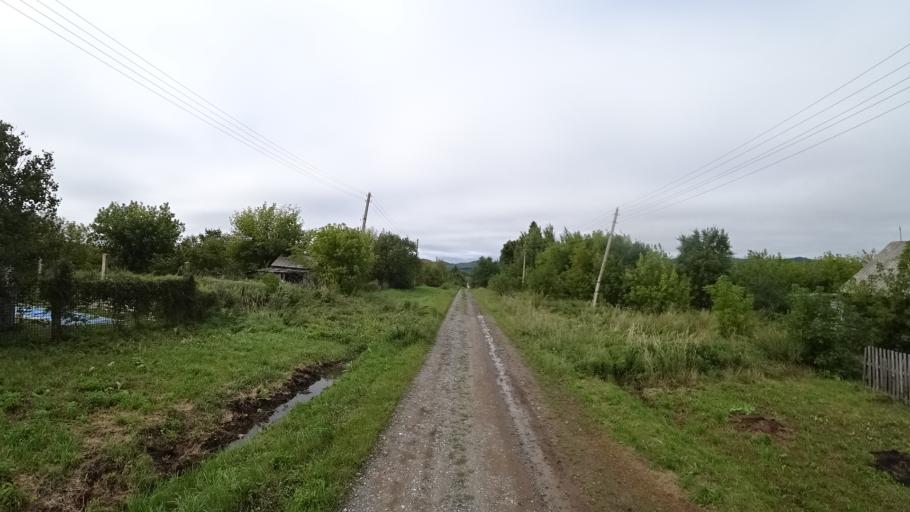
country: RU
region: Primorskiy
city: Lyalichi
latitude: 44.0762
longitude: 132.4840
